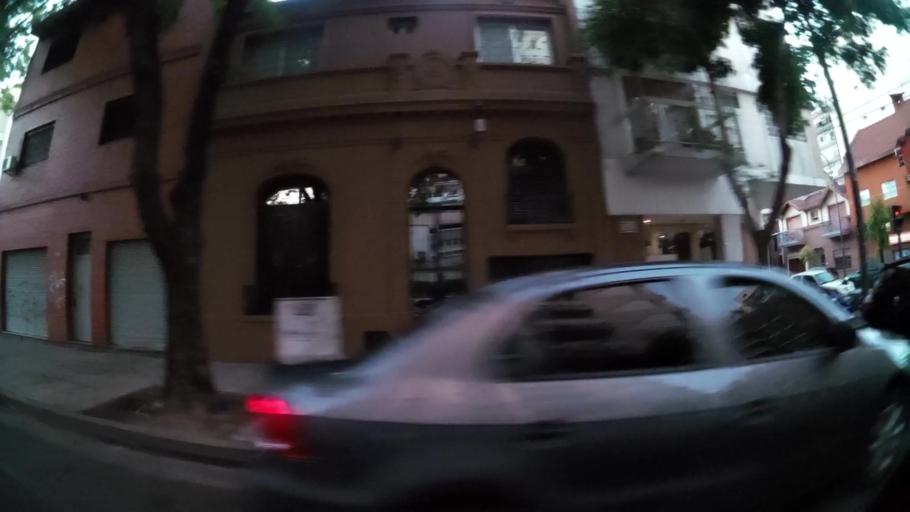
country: AR
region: Buenos Aires F.D.
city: Villa Santa Rita
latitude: -34.6361
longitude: -58.4386
